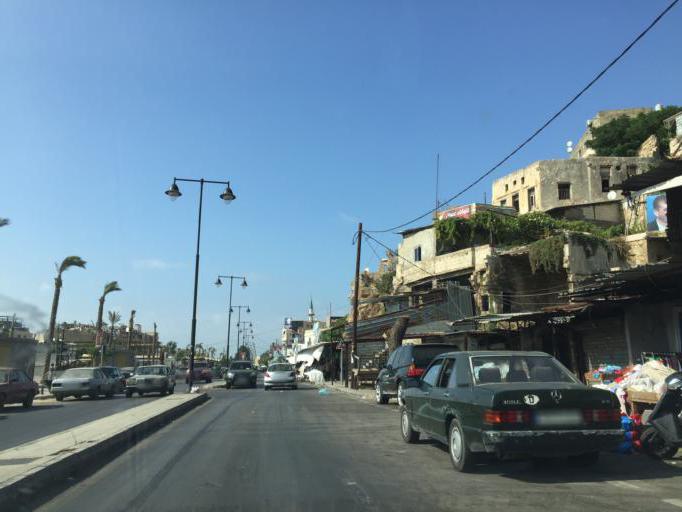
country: LB
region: Liban-Nord
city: Tripoli
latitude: 34.4368
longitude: 35.8470
